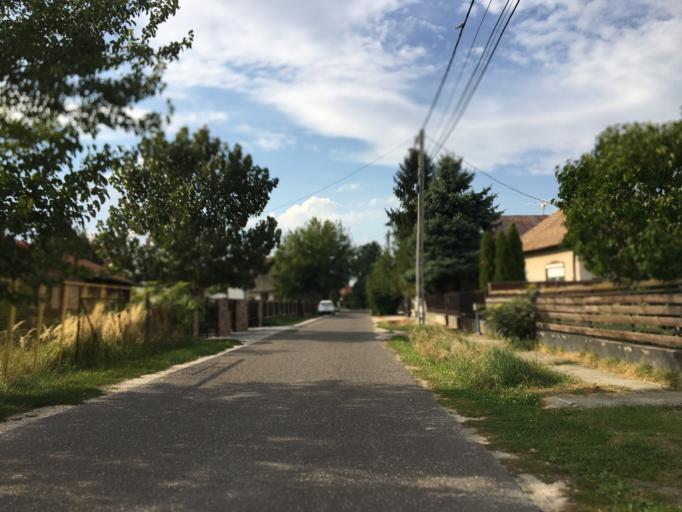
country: HU
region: Pest
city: Szigetszentmiklos
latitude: 47.3503
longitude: 19.0504
